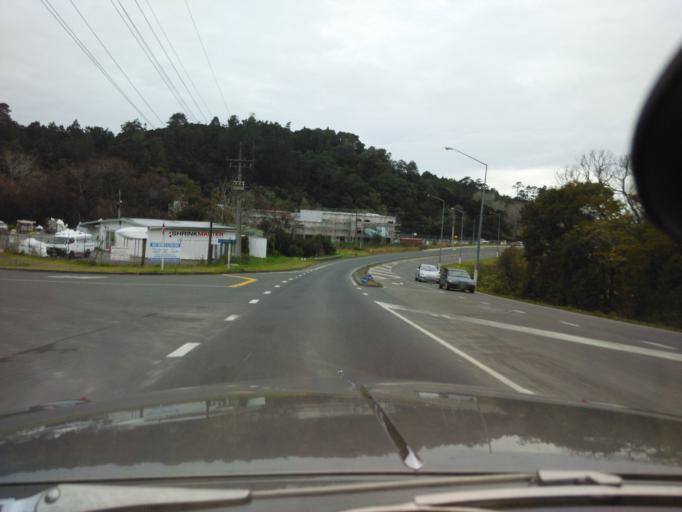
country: NZ
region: Auckland
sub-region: Auckland
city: Rothesay Bay
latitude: -36.7215
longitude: 174.6887
